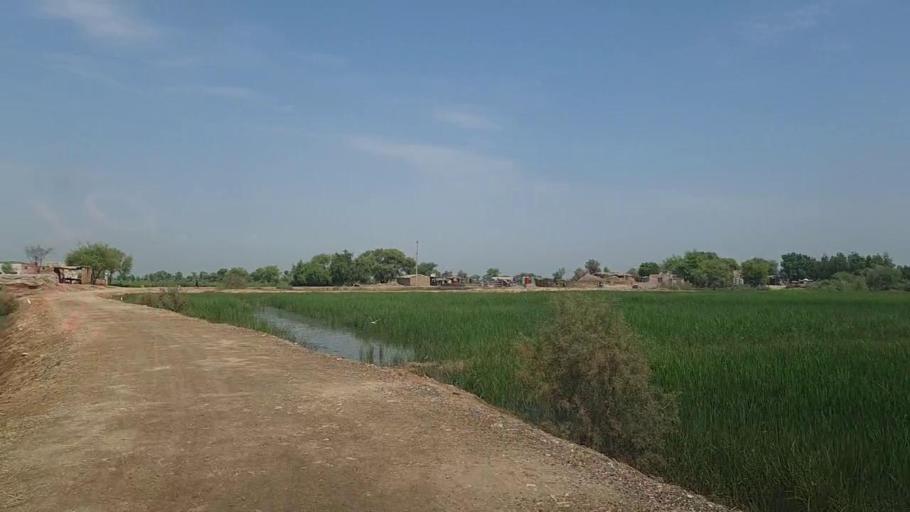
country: PK
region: Sindh
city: Thul
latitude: 28.3063
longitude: 68.6831
